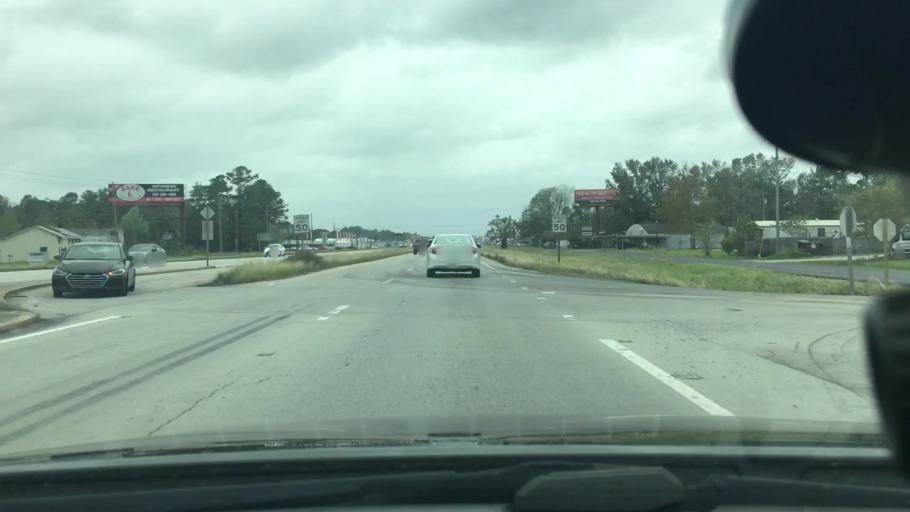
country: US
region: North Carolina
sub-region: Craven County
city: James City
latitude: 35.0649
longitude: -77.0224
